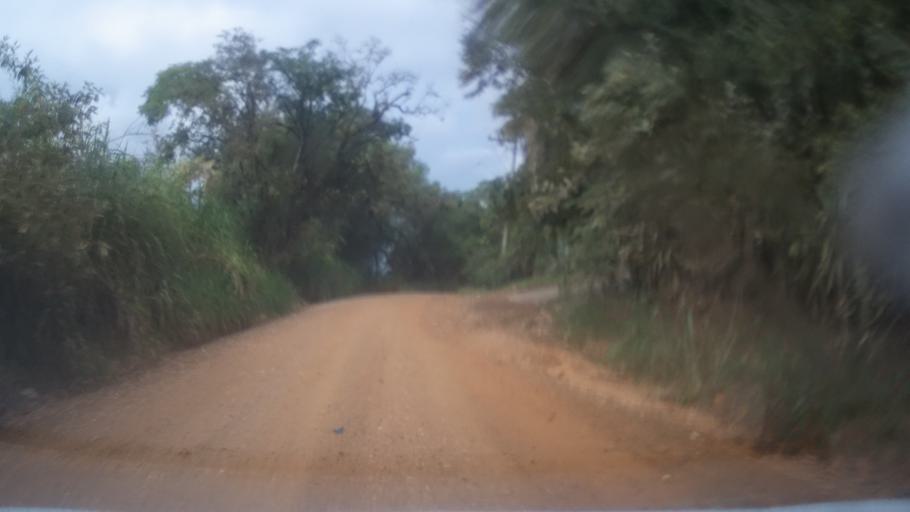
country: BR
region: Sao Paulo
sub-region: Itupeva
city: Itupeva
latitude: -23.1917
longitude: -47.0071
